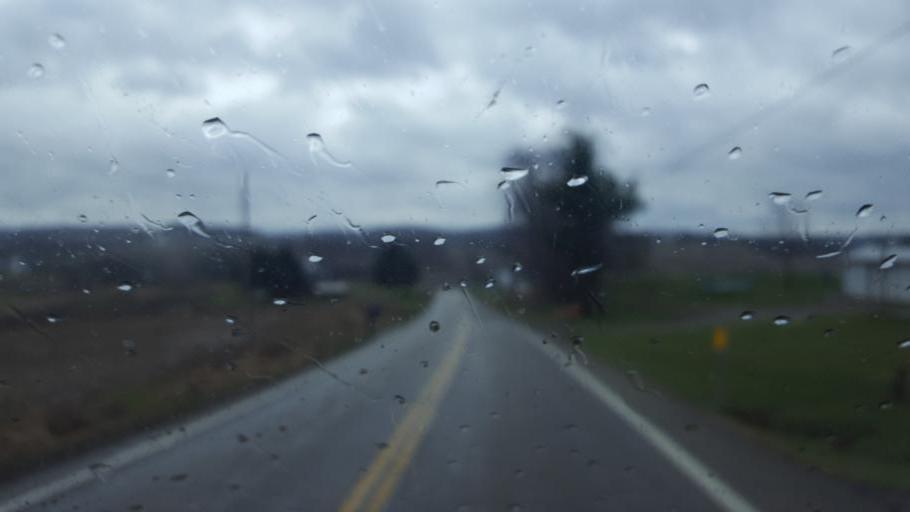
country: US
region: Ohio
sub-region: Ashland County
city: Loudonville
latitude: 40.6028
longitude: -82.1282
